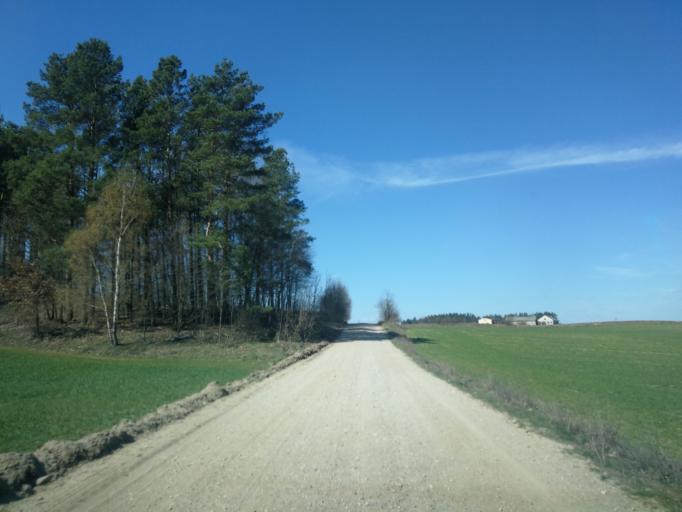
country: PL
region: Warmian-Masurian Voivodeship
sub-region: Powiat dzialdowski
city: Rybno
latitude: 53.4410
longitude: 19.9380
